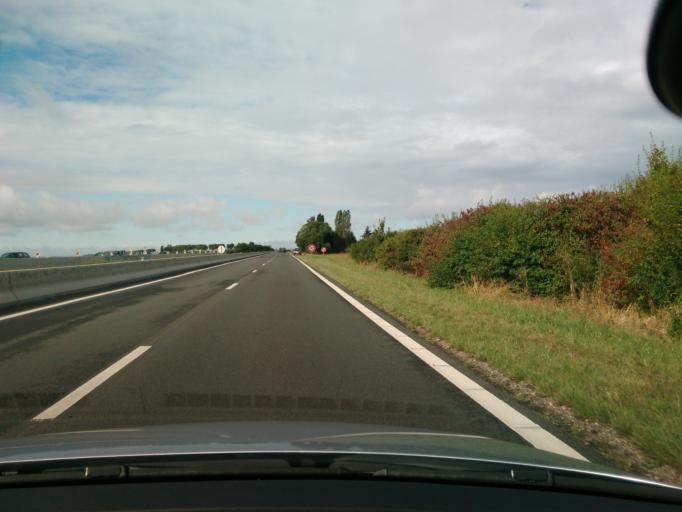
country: FR
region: Centre
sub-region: Departement d'Eure-et-Loir
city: Bu
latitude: 48.7603
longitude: 1.5144
